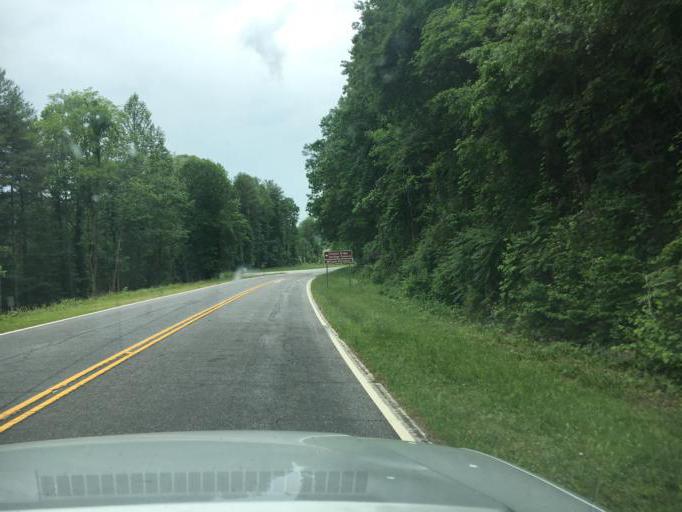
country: US
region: South Carolina
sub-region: Greenville County
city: Tigerville
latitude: 35.1344
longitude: -82.4196
